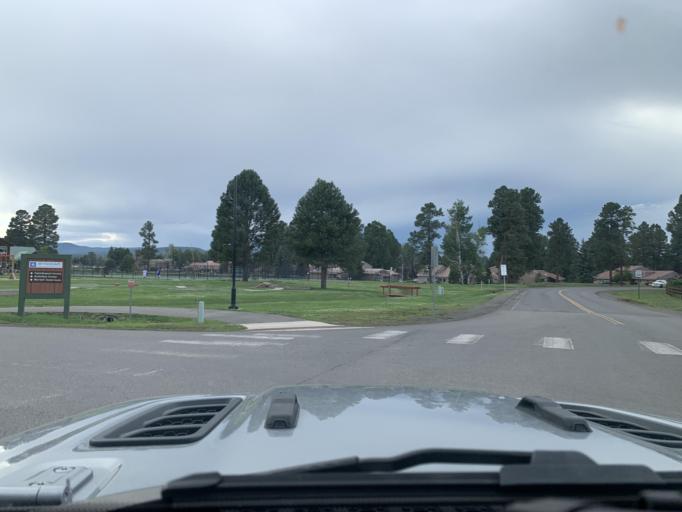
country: US
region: Colorado
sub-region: Archuleta County
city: Pagosa Springs
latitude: 37.2593
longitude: -107.0704
